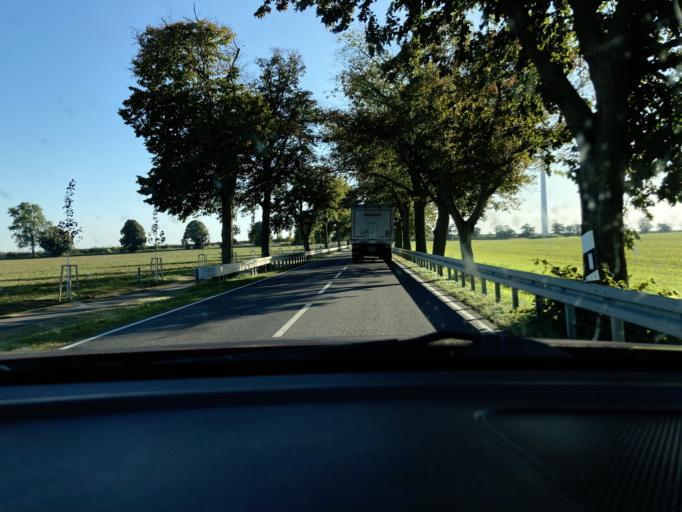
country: DE
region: Mecklenburg-Vorpommern
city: Alt-Sanitz
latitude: 53.7762
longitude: 13.6549
